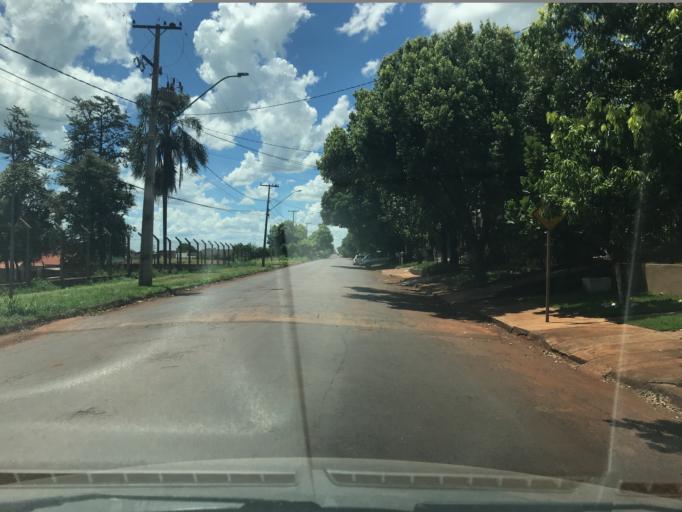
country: BR
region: Parana
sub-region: Palotina
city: Palotina
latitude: -24.2793
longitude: -53.8485
